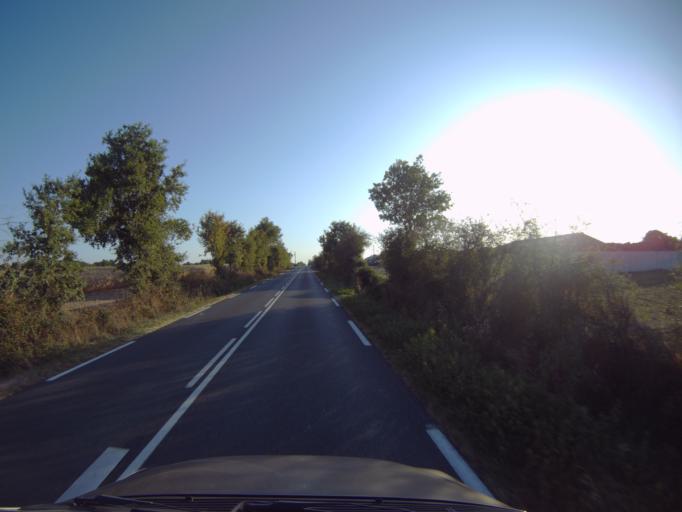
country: FR
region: Pays de la Loire
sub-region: Departement de la Vendee
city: La Bernardiere
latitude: 47.0345
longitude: -1.2589
